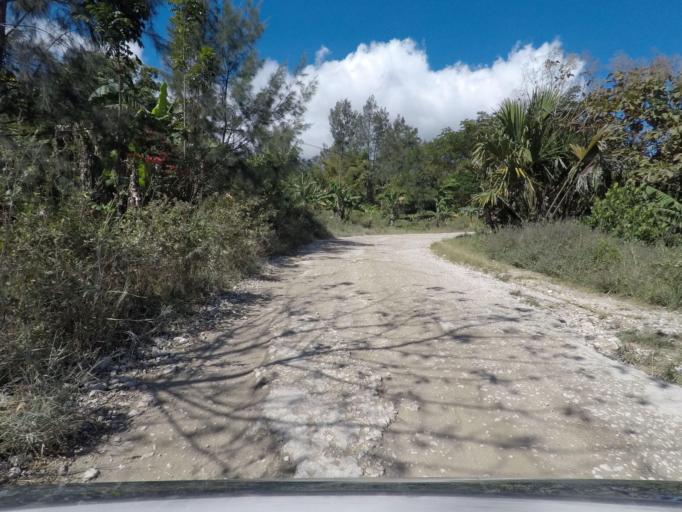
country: TL
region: Baucau
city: Venilale
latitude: -8.6686
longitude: 126.3679
